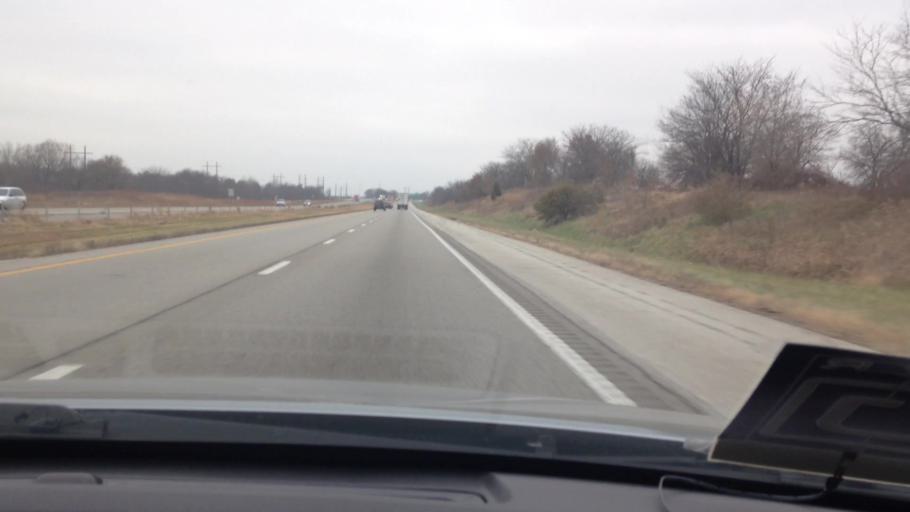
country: US
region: Missouri
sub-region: Cass County
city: Raymore
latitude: 38.7745
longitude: -94.4933
